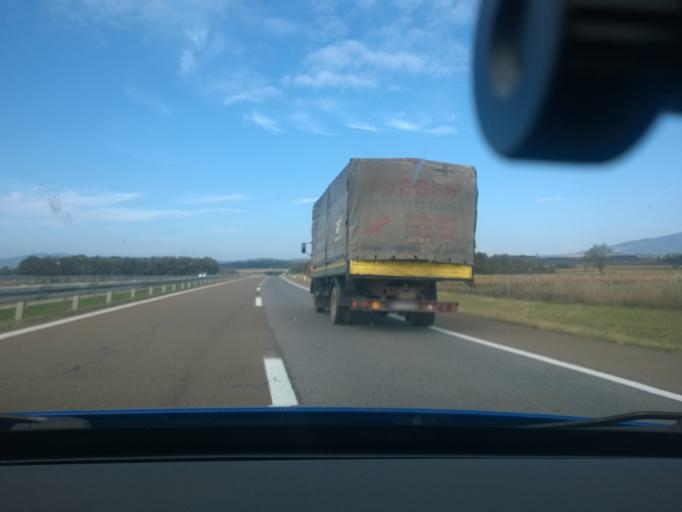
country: RS
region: Central Serbia
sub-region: Nisavski Okrug
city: Aleksinac
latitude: 43.5937
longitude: 21.6414
